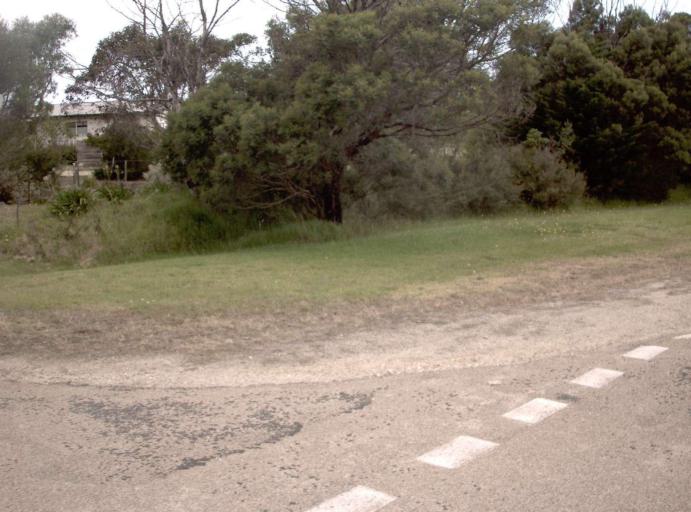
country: AU
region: Victoria
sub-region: Wellington
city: Sale
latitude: -38.1924
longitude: 147.0939
